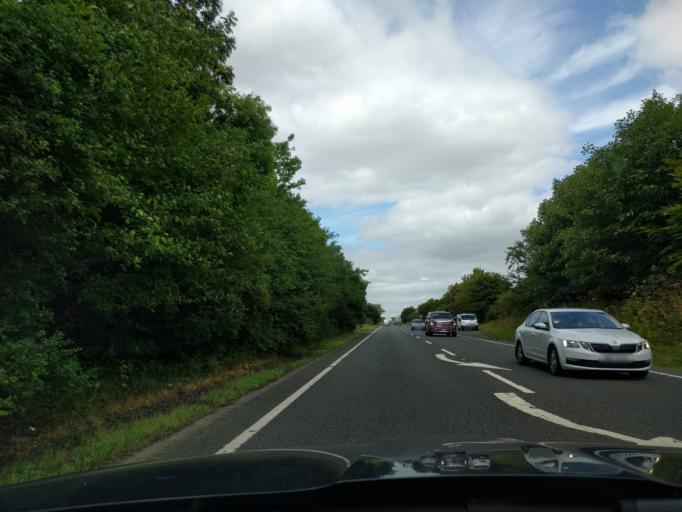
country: GB
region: England
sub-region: Northumberland
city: Alnwick
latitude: 55.4356
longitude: -1.6932
